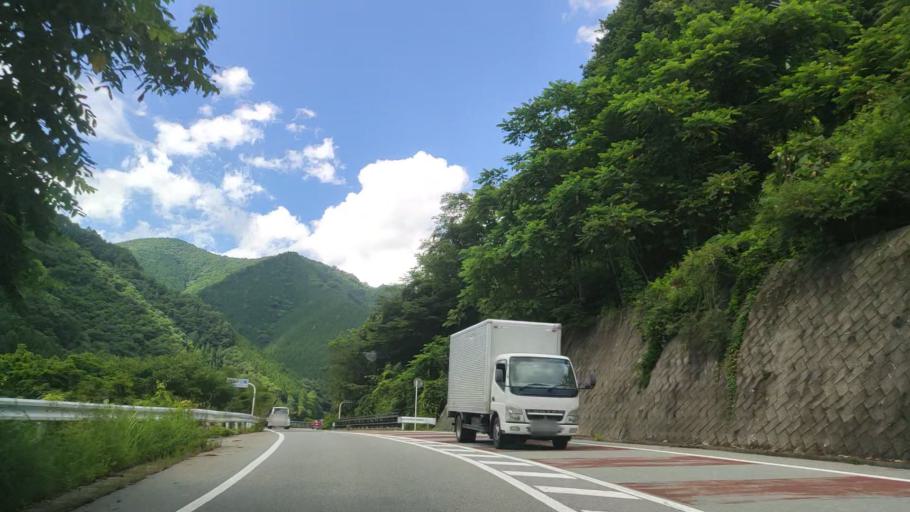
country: JP
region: Yamanashi
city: Enzan
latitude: 35.8178
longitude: 138.7572
